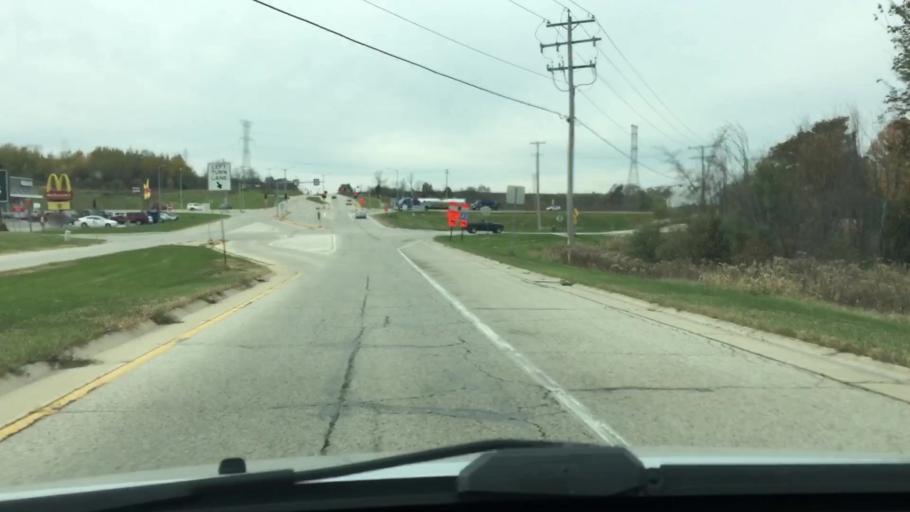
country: US
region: Wisconsin
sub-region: Waukesha County
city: Big Bend
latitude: 42.9146
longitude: -88.2169
